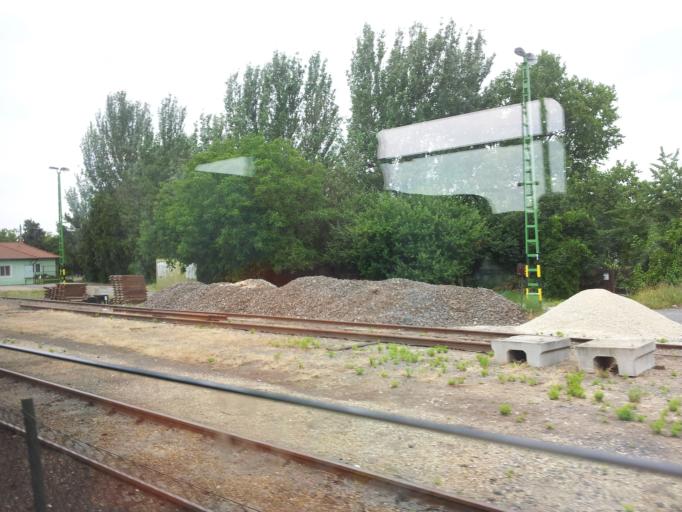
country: HU
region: Veszprem
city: Balatonfured
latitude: 46.9557
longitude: 17.8817
